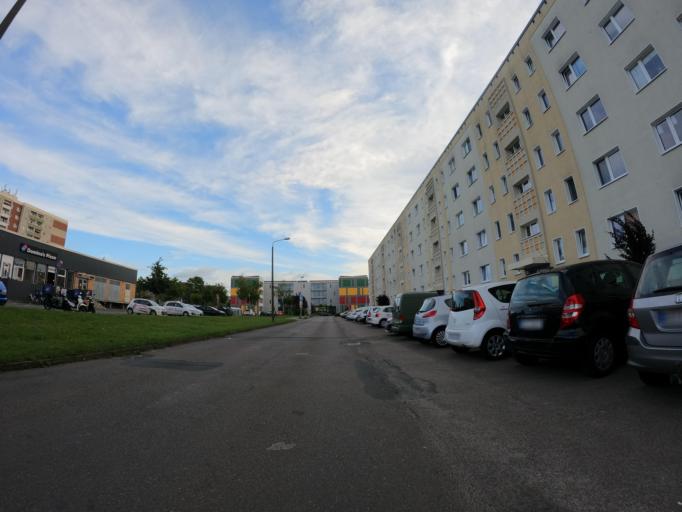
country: DE
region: Mecklenburg-Vorpommern
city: Kramerhof
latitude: 54.3246
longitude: 13.0538
